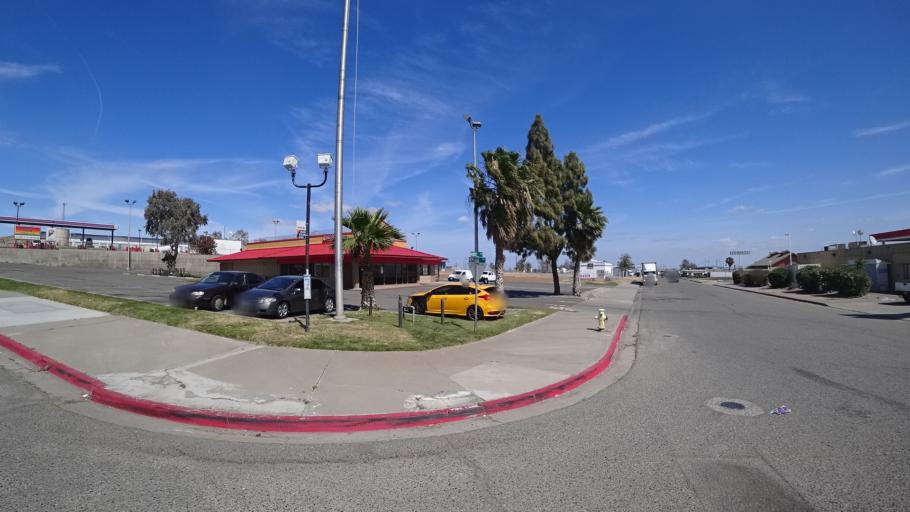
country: US
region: California
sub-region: Kings County
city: Kettleman City
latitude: 35.9882
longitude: -119.9606
